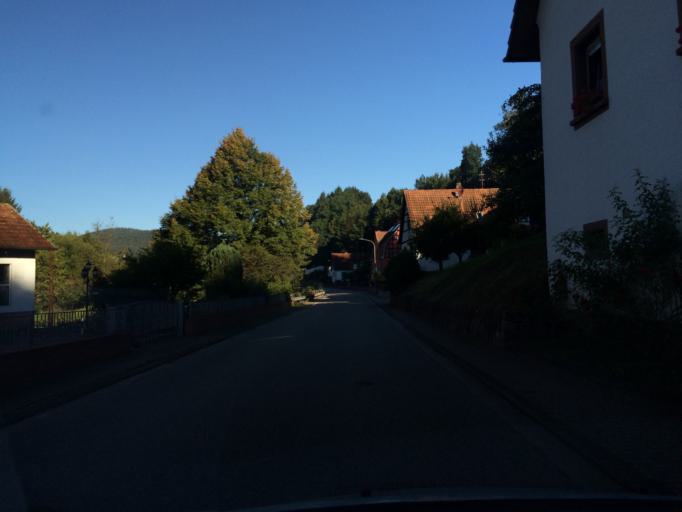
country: DE
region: Rheinland-Pfalz
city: Bobenthal
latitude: 49.0613
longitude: 7.8620
